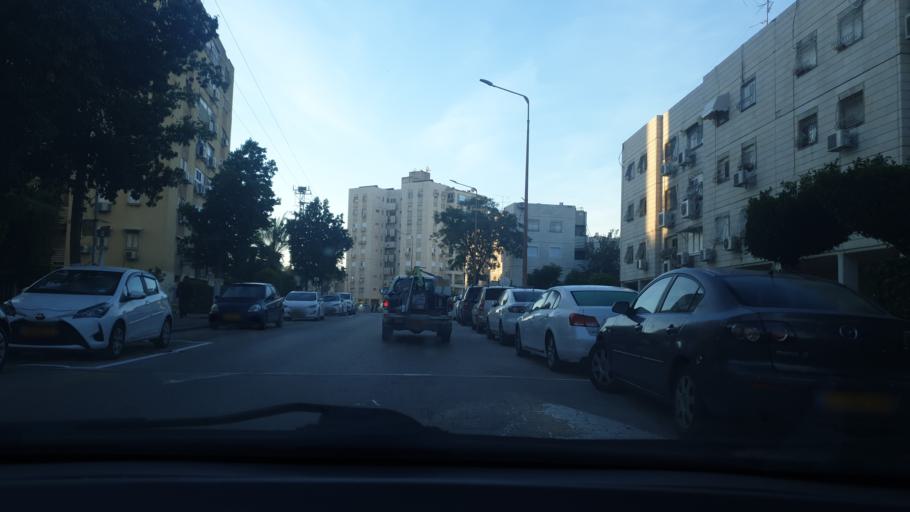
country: IL
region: Central District
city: Ramla
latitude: 31.9360
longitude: 34.8578
